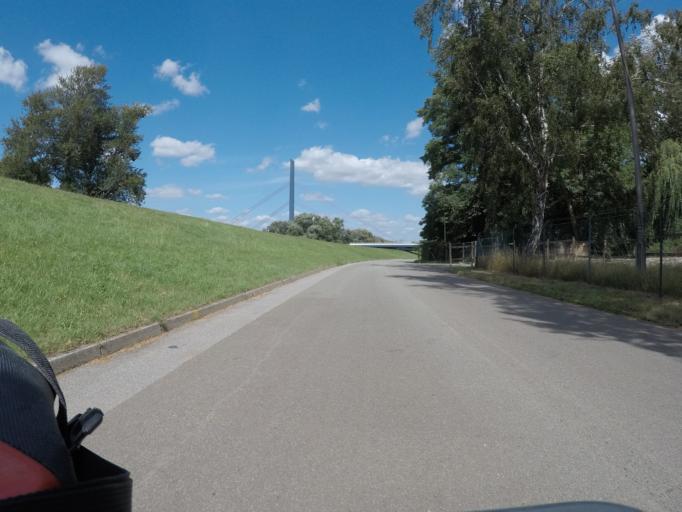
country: DE
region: Hamburg
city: Rothenburgsort
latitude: 53.5072
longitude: 10.0622
